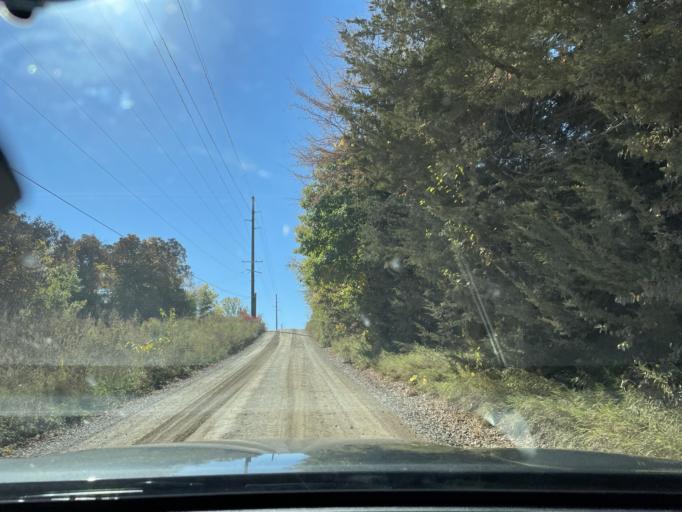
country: US
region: Missouri
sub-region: Andrew County
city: Savannah
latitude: 39.9258
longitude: -94.8612
